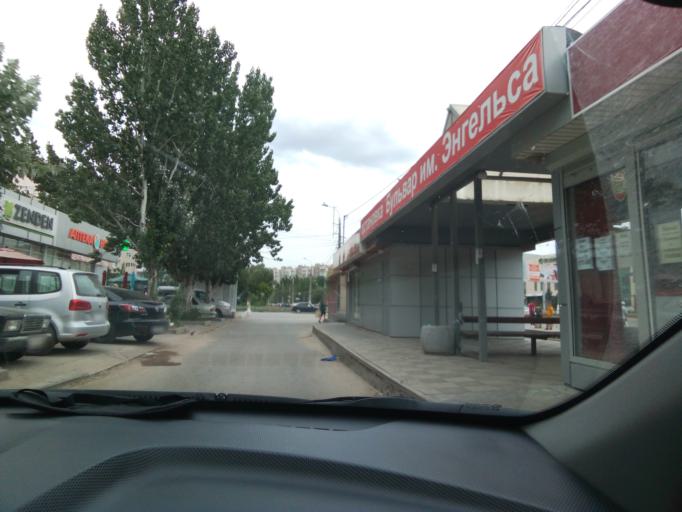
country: RU
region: Volgograd
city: Krasnoslobodsk
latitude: 48.5143
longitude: 44.5412
